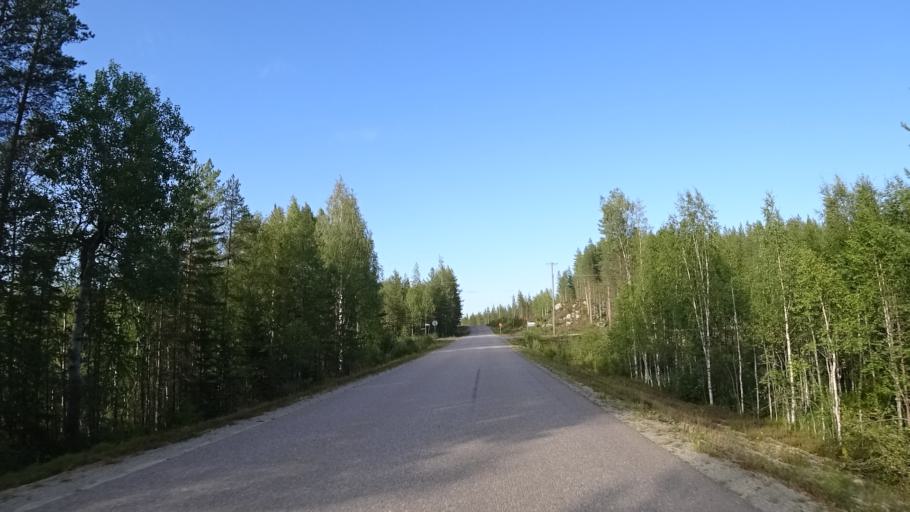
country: FI
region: North Karelia
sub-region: Joensuu
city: Eno
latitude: 63.0640
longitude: 30.5546
